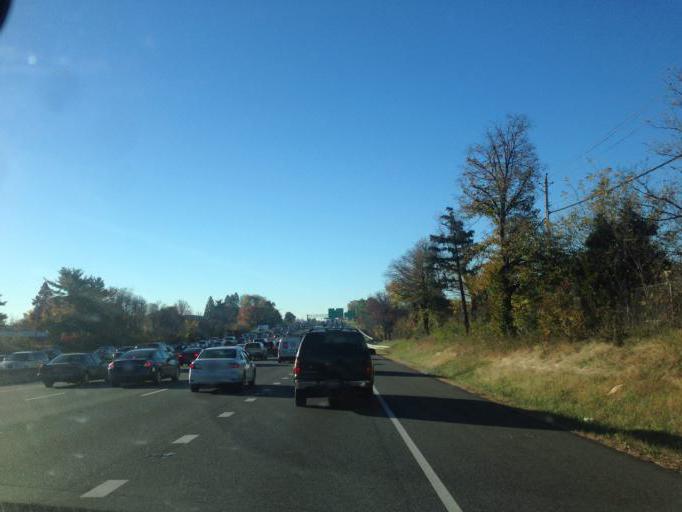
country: US
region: Maryland
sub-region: Baltimore County
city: Woodlawn
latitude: 39.3191
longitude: -76.7450
